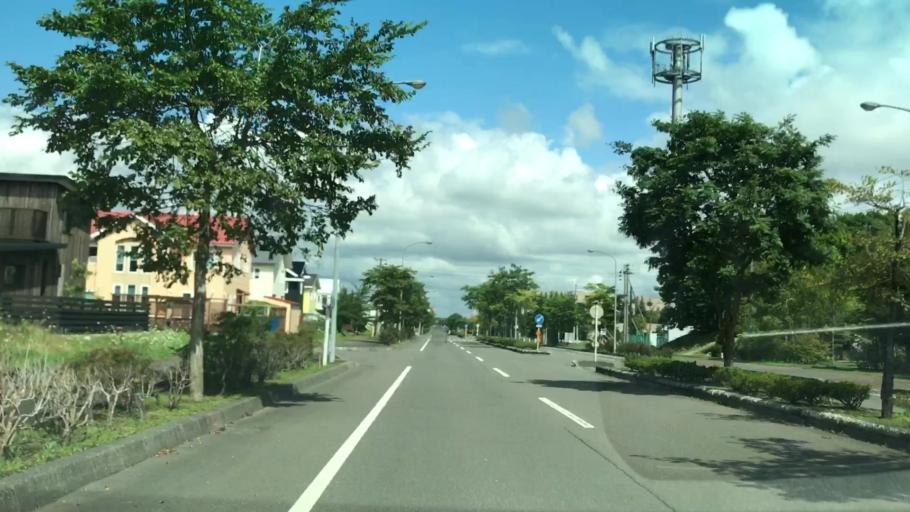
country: JP
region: Hokkaido
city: Chitose
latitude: 42.7777
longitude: 141.5997
